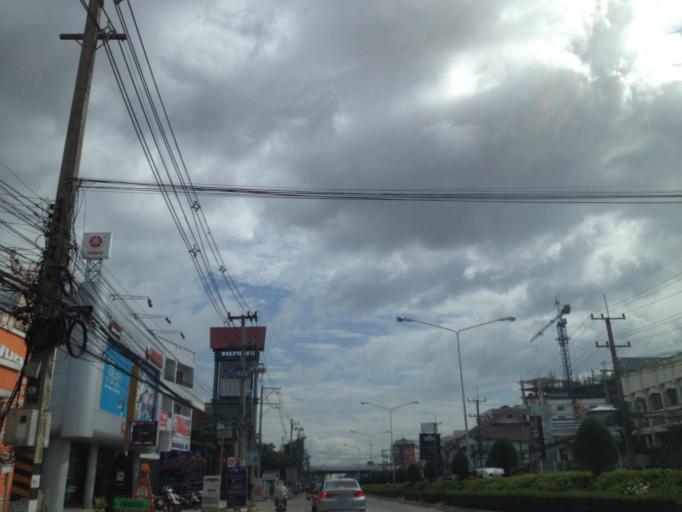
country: TH
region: Chiang Mai
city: Chiang Mai
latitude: 18.7666
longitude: 98.9756
